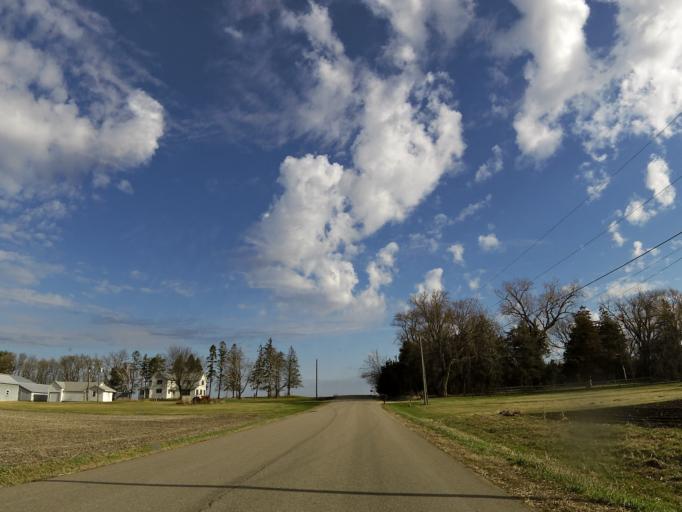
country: US
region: Minnesota
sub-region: Dakota County
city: Hastings
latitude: 44.7974
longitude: -92.8423
